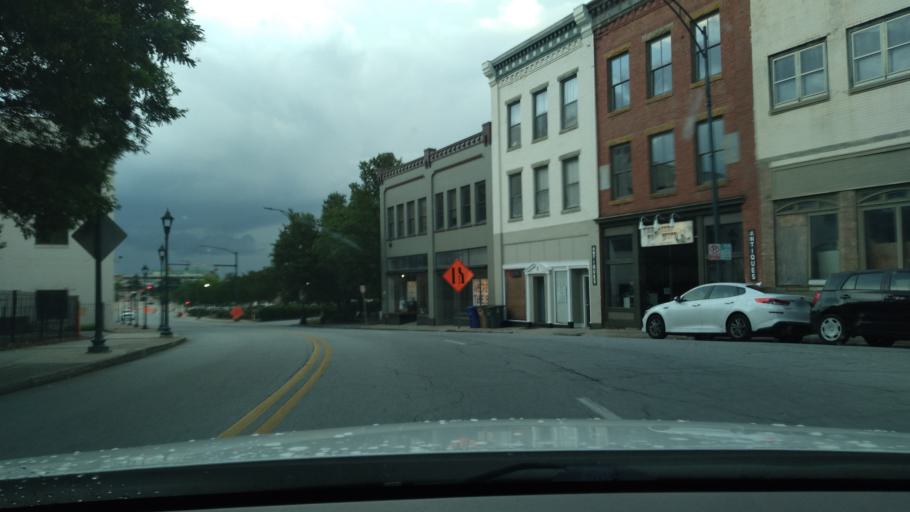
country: US
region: North Carolina
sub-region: Guilford County
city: Greensboro
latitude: 36.0684
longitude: -79.7895
